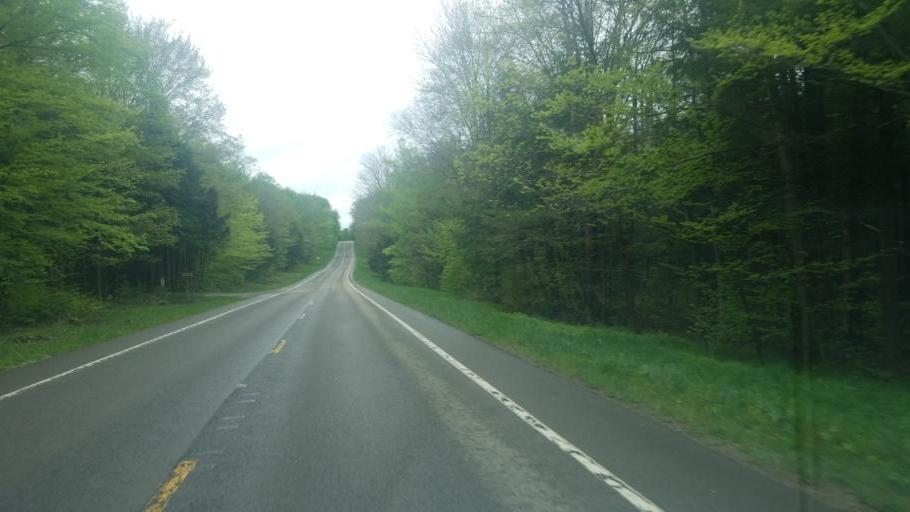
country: US
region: Pennsylvania
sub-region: Warren County
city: Sheffield
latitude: 41.5575
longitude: -78.9996
